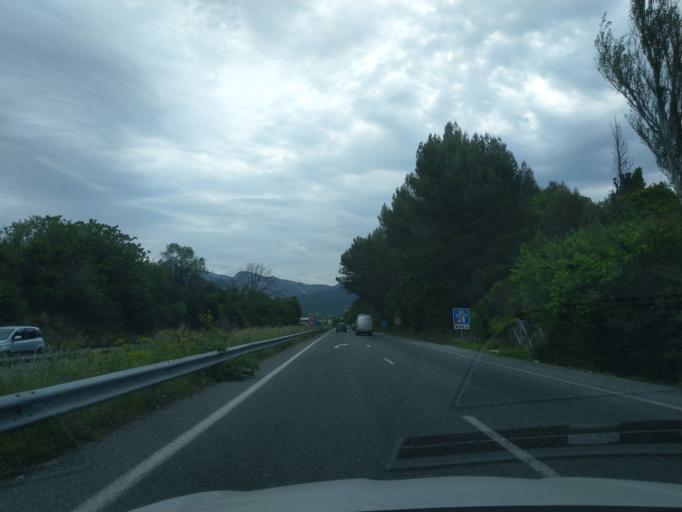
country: FR
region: Provence-Alpes-Cote d'Azur
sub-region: Departement des Bouches-du-Rhone
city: Aubagne
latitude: 43.2839
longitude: 5.5882
